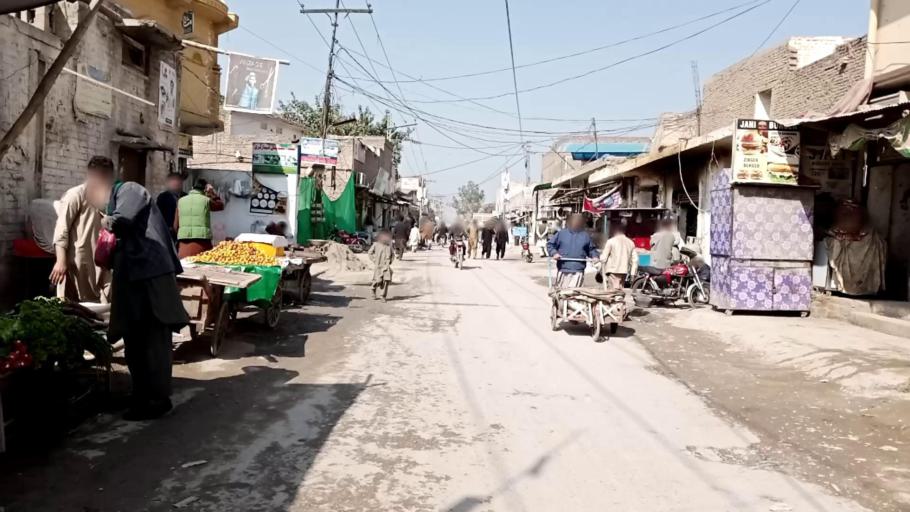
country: PK
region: Khyber Pakhtunkhwa
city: Peshawar
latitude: 34.0093
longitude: 71.5186
